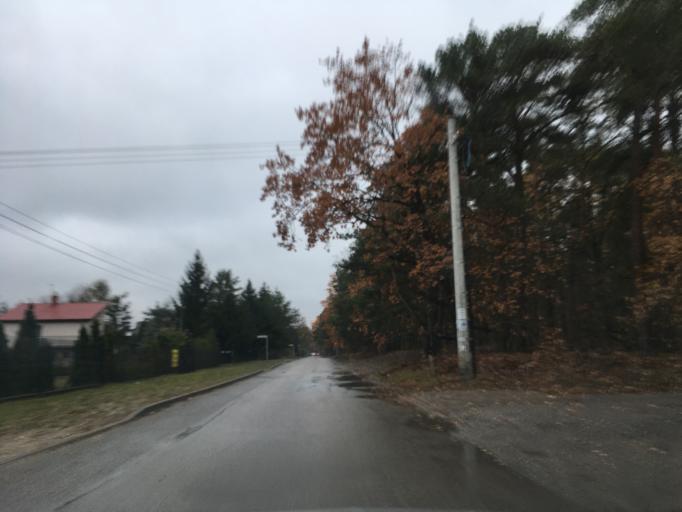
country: PL
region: Masovian Voivodeship
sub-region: Powiat piaseczynski
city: Lesznowola
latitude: 52.0914
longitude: 20.8900
